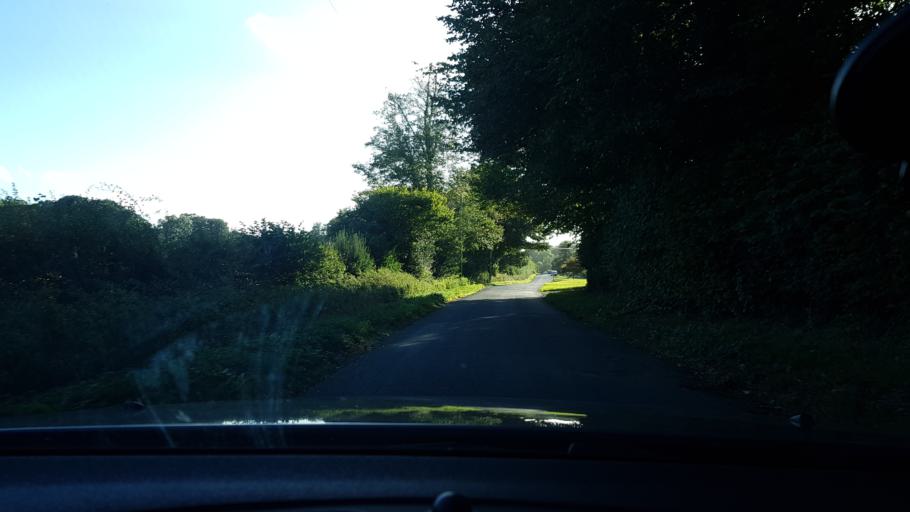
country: GB
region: England
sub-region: West Berkshire
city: Wickham
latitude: 51.4465
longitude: -1.4262
